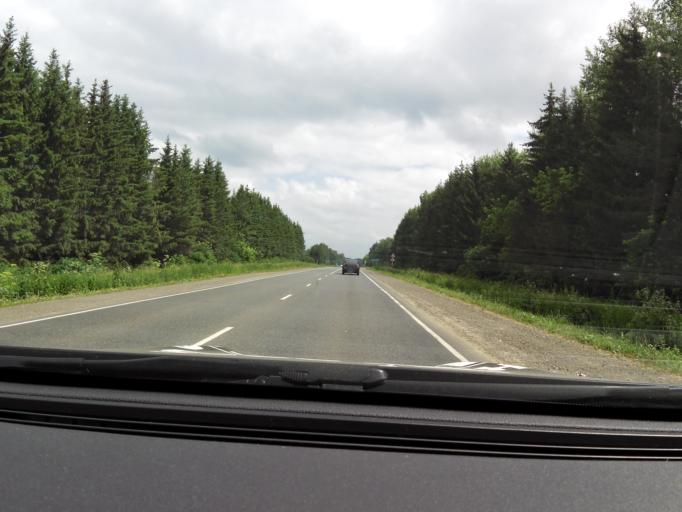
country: RU
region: Perm
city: Kungur
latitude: 57.4522
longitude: 56.7907
